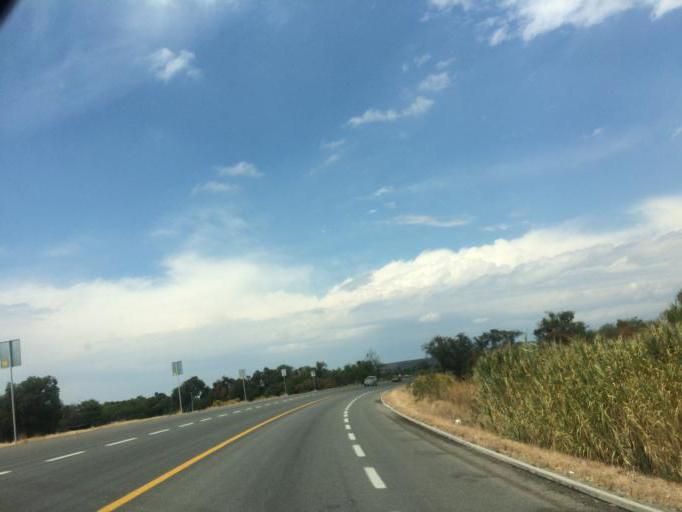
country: MX
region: Guanajuato
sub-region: Silao de la Victoria
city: Loma de Yerbabuena
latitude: 21.0279
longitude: -101.4573
